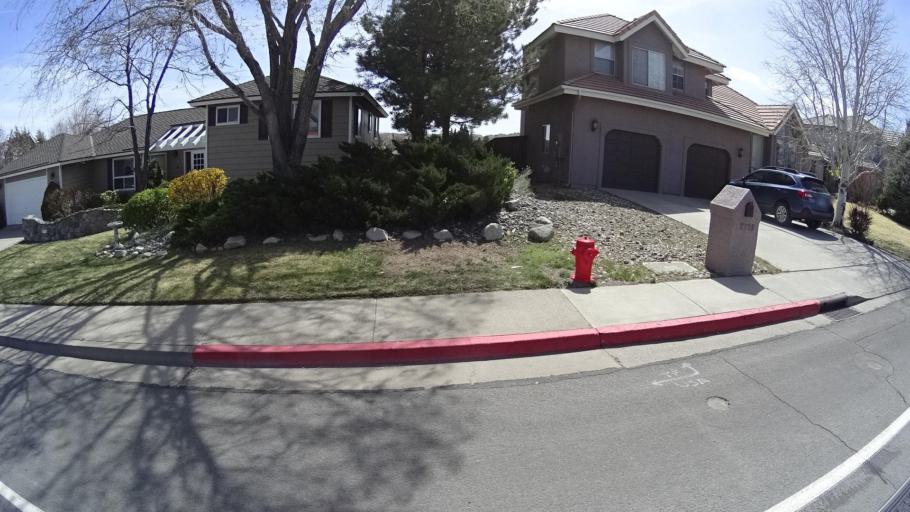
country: US
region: Nevada
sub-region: Washoe County
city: Reno
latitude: 39.4867
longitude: -119.8467
